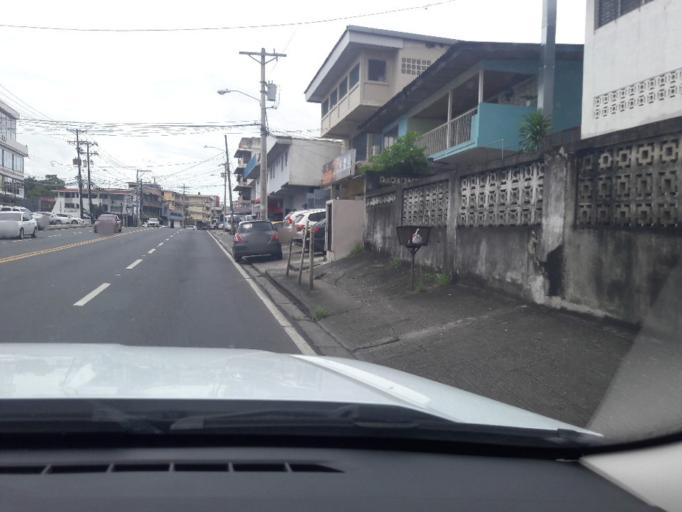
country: PA
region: Panama
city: Panama
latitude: 9.0130
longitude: -79.5219
